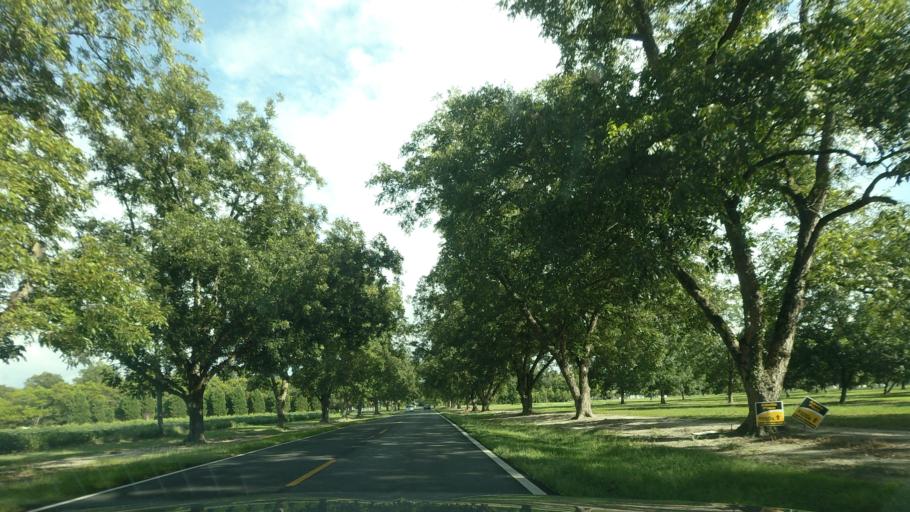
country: US
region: Georgia
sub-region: Peach County
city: Byron
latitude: 32.6403
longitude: -83.7398
